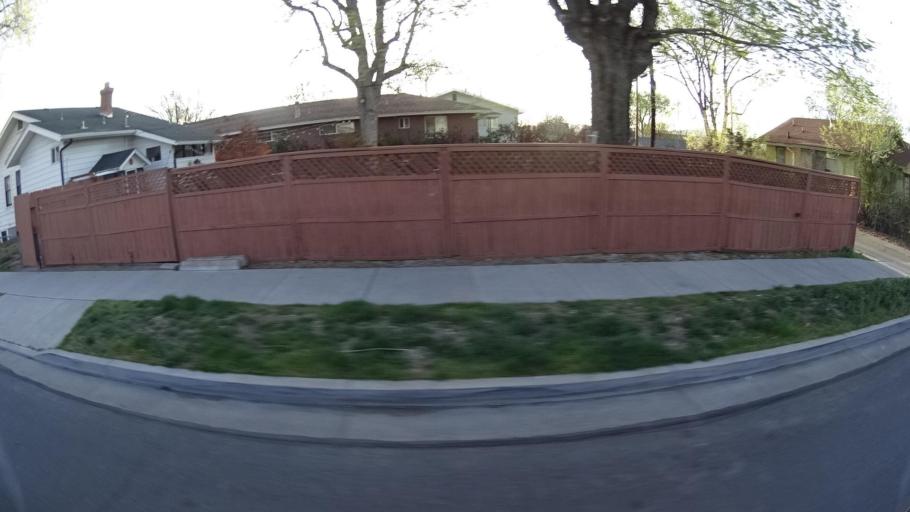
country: US
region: Nevada
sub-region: Washoe County
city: Reno
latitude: 39.5198
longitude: -119.8005
